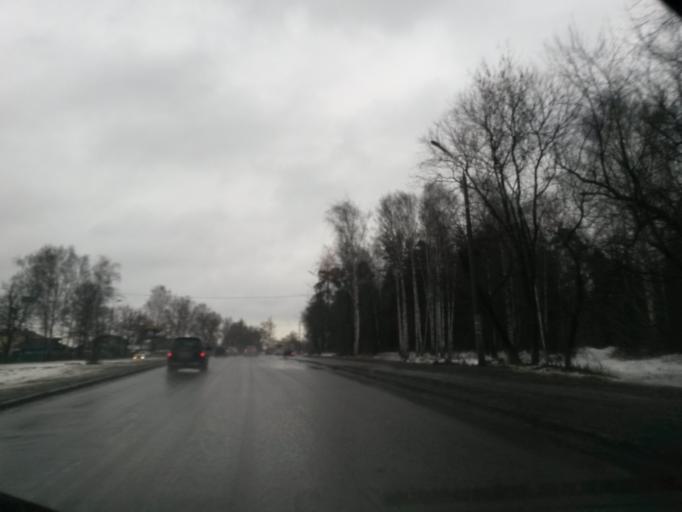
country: RU
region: Jaroslavl
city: Yaroslavl
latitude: 57.6447
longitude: 39.9200
